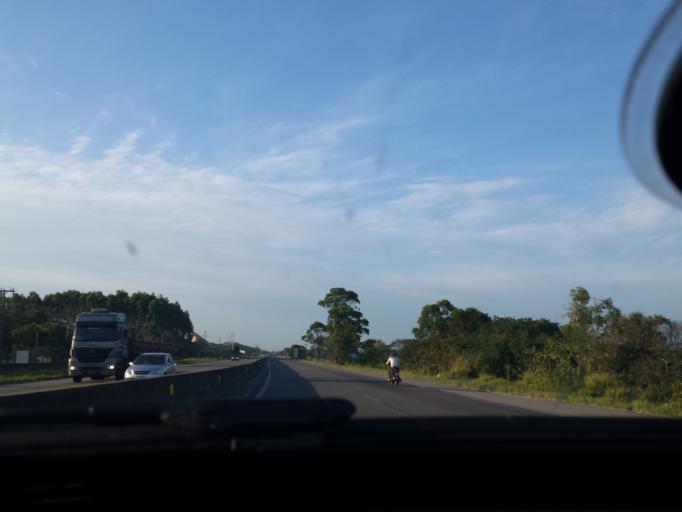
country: BR
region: Santa Catarina
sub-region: Imbituba
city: Imbituba
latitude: -28.3025
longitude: -48.7199
